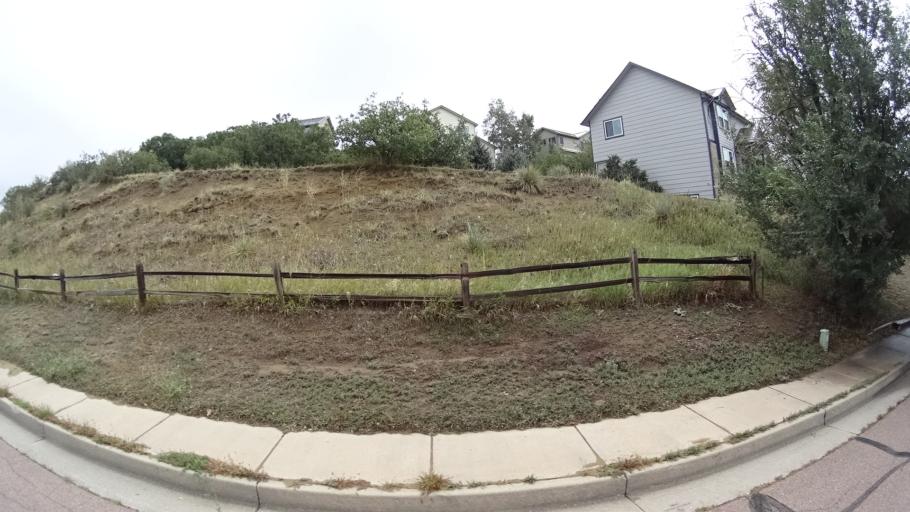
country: US
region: Colorado
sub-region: El Paso County
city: Cimarron Hills
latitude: 38.9219
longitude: -104.7596
